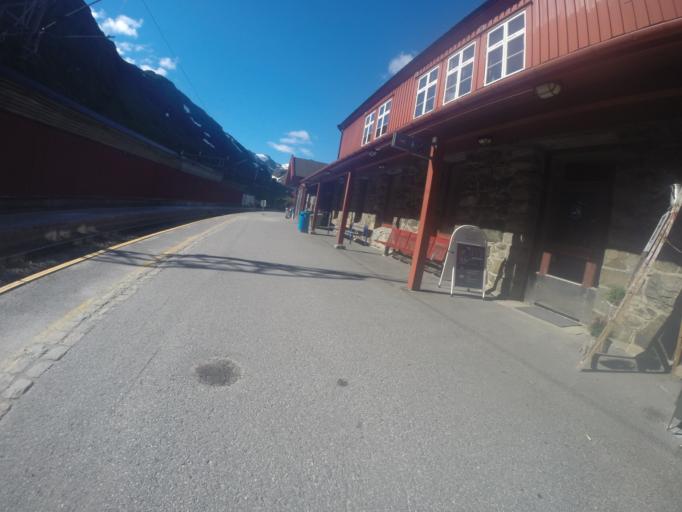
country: NO
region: Sogn og Fjordane
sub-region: Aurland
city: Aurlandsvangen
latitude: 60.7354
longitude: 7.1230
